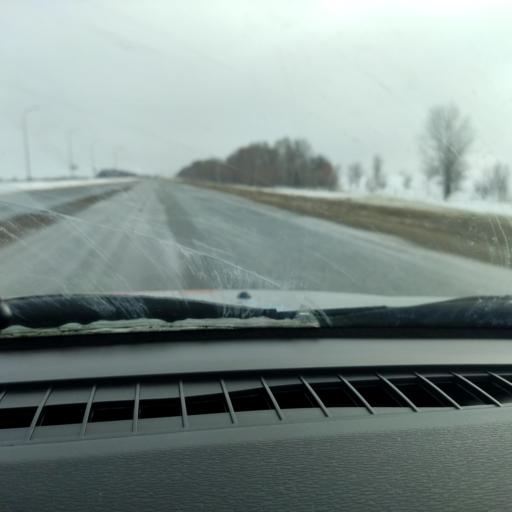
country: RU
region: Samara
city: Dubovyy Umet
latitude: 53.0105
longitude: 50.2415
